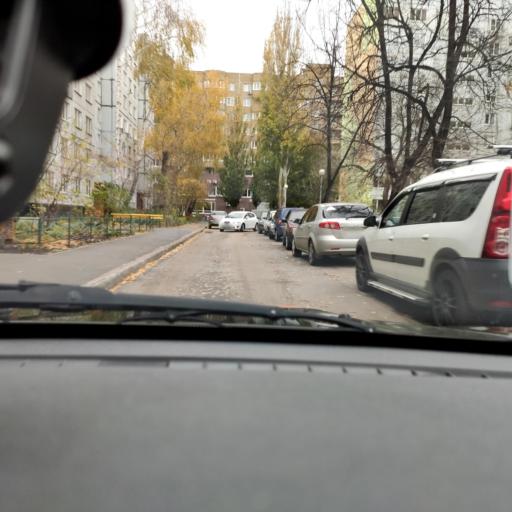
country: RU
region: Samara
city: Tol'yatti
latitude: 53.5206
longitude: 49.2831
